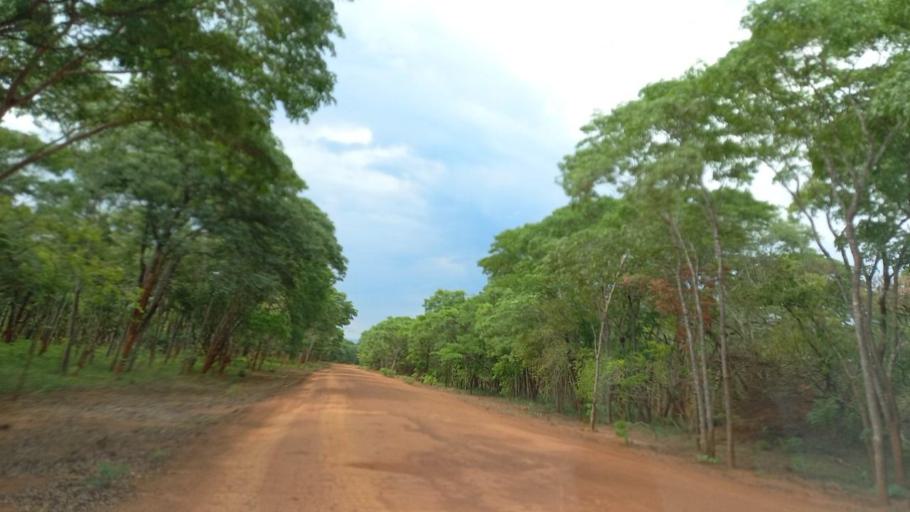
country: ZM
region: North-Western
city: Kalengwa
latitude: -13.4099
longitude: 25.0627
